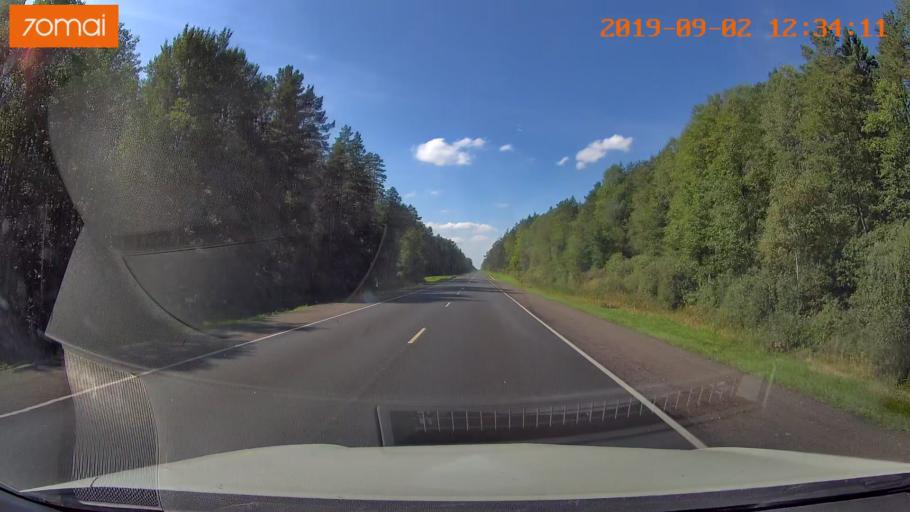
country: RU
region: Smolensk
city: Shumyachi
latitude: 53.8122
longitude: 32.4104
